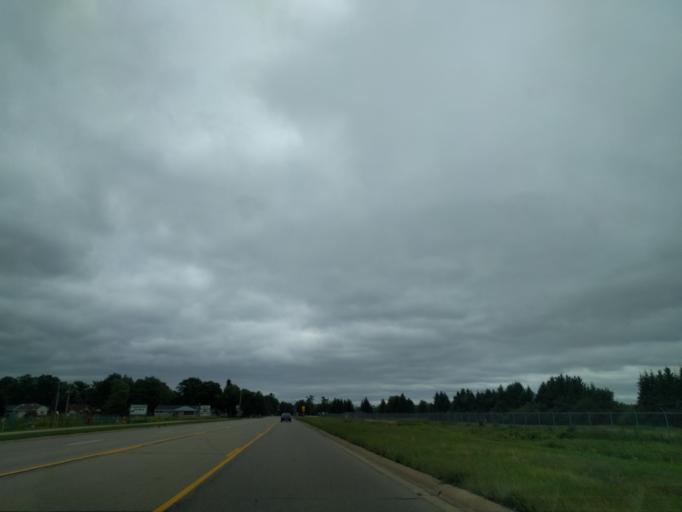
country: US
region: Michigan
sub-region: Delta County
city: Escanaba
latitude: 45.7212
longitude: -87.0801
